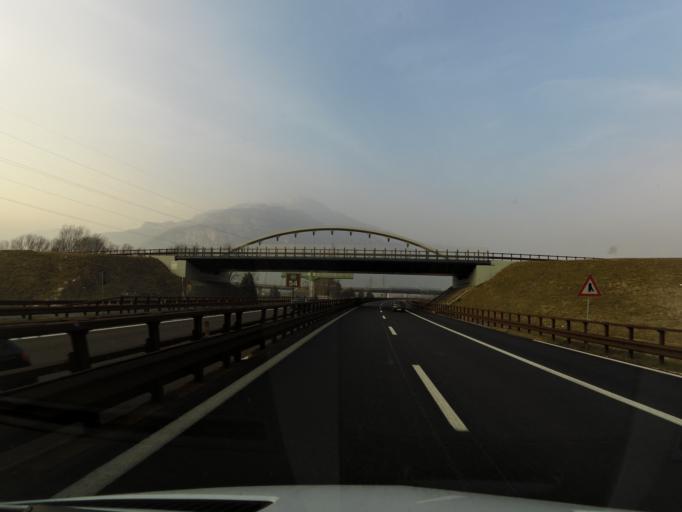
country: IT
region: Trentino-Alto Adige
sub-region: Provincia di Trento
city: Marco
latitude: 45.8436
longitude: 11.0005
